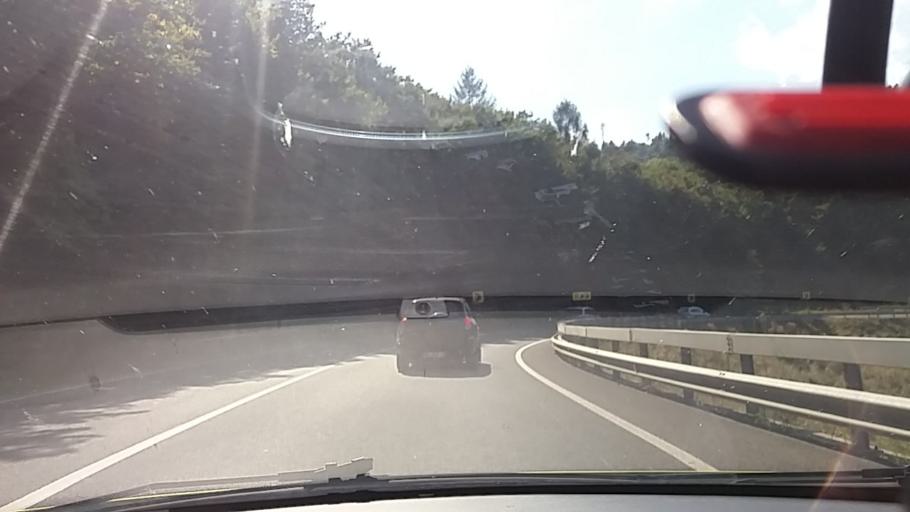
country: RO
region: Sibiu
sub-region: Comuna Slimnic
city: Slimnic
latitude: 45.9394
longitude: 24.1706
